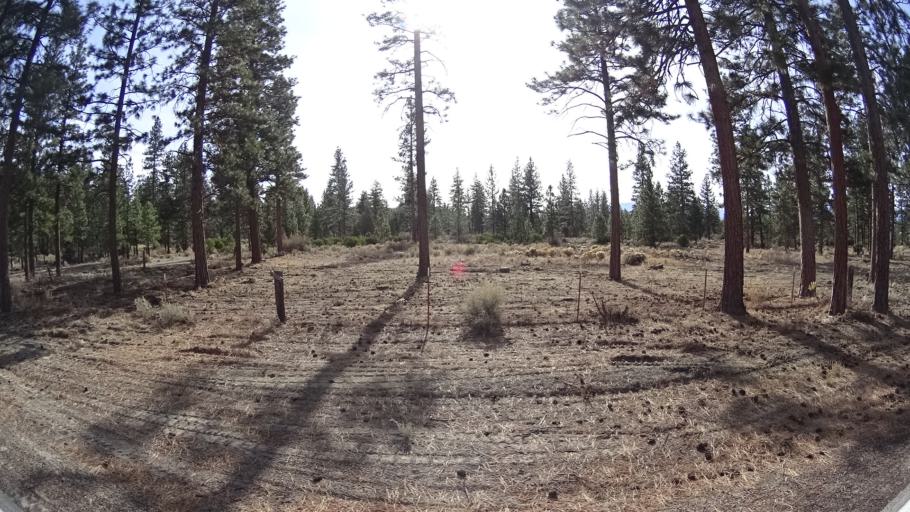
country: US
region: California
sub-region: Siskiyou County
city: Weed
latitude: 41.4940
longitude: -122.3769
